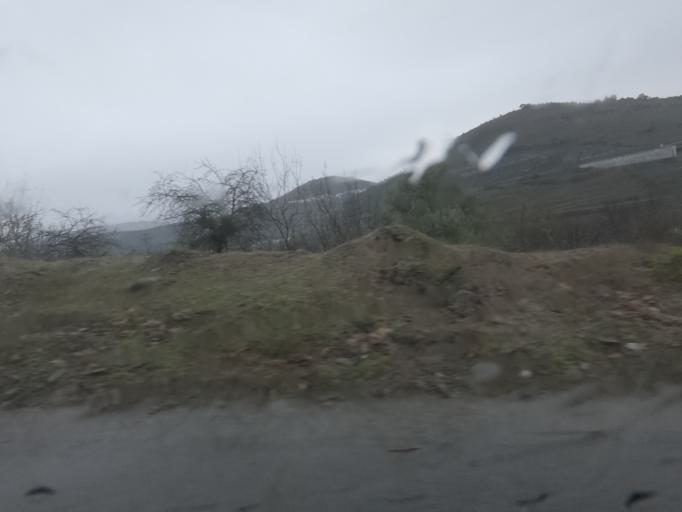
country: PT
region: Vila Real
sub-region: Peso da Regua
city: Peso da Regua
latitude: 41.1691
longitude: -7.7544
